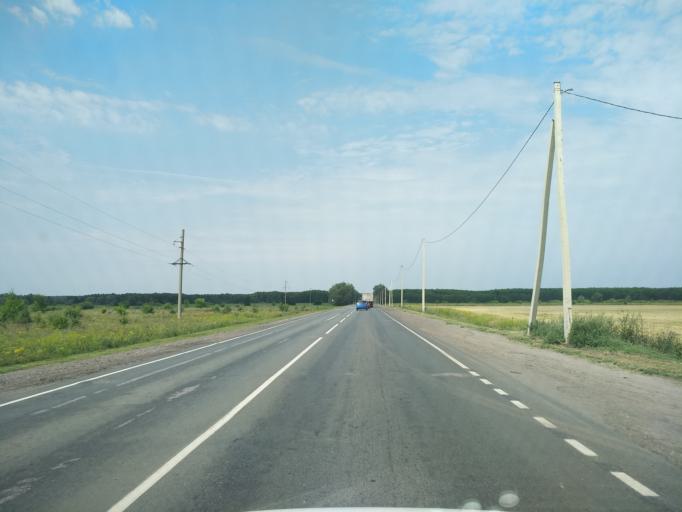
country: RU
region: Voronezj
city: Orlovo
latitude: 51.6804
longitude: 39.6086
